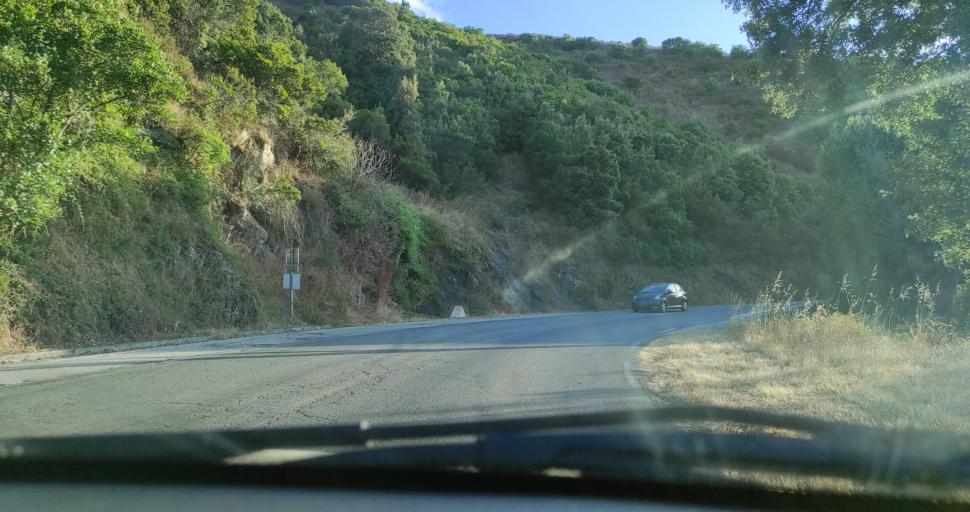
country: FR
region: Corsica
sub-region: Departement de la Corse-du-Sud
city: Appietto
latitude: 42.0219
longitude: 8.7417
